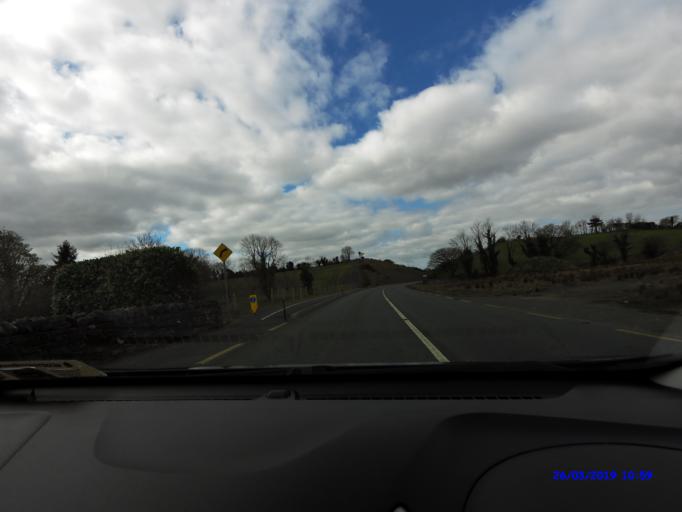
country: IE
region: Connaught
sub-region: Maigh Eo
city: Castlebar
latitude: 53.8490
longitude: -9.3467
